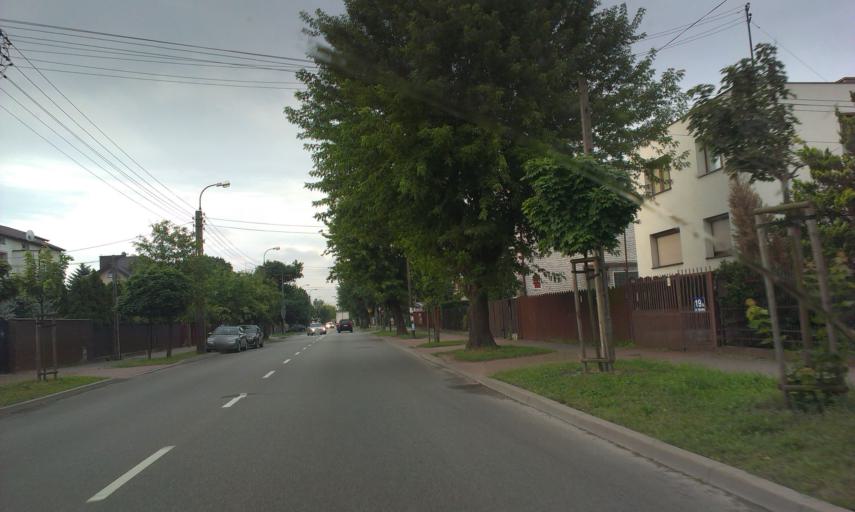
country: PL
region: Masovian Voivodeship
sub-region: Warszawa
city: Ursus
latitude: 52.1855
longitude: 20.8849
